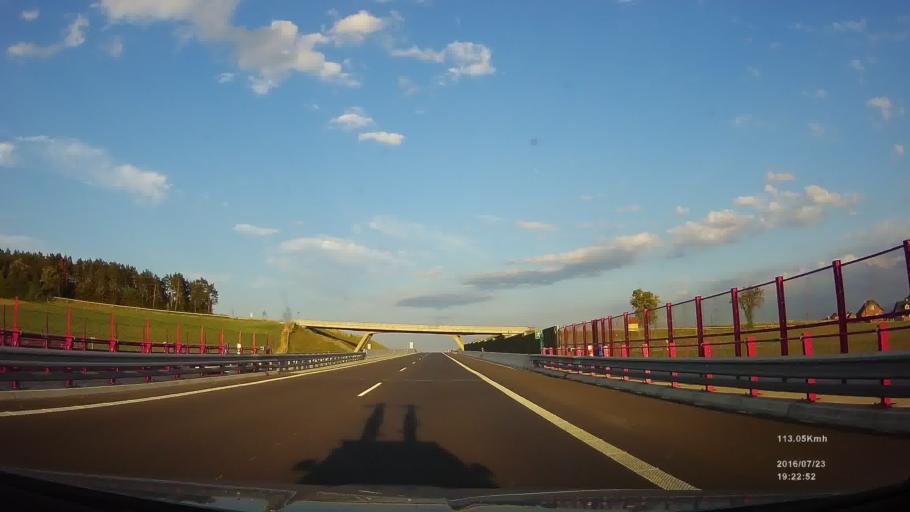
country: SK
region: Presovsky
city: Lubica
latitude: 49.0067
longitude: 20.4681
